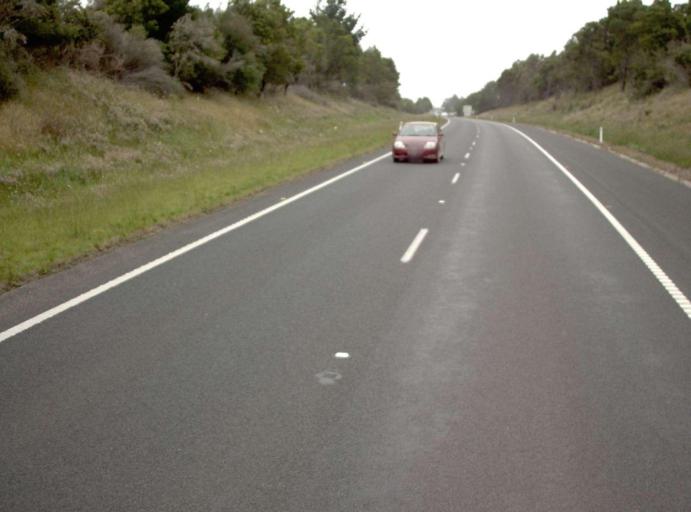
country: AU
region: Victoria
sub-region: Baw Baw
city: Warragul
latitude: -38.1834
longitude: 145.9911
